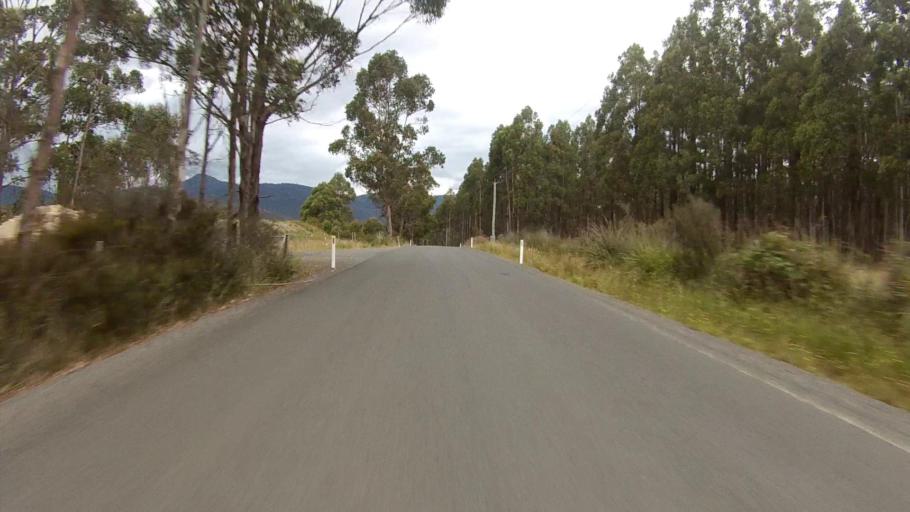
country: AU
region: Tasmania
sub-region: Huon Valley
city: Huonville
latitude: -42.9665
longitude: 147.0847
